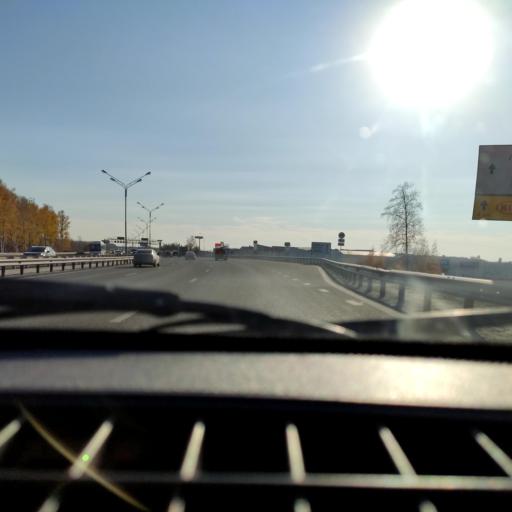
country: RU
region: Bashkortostan
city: Ufa
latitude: 54.6805
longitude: 55.9357
